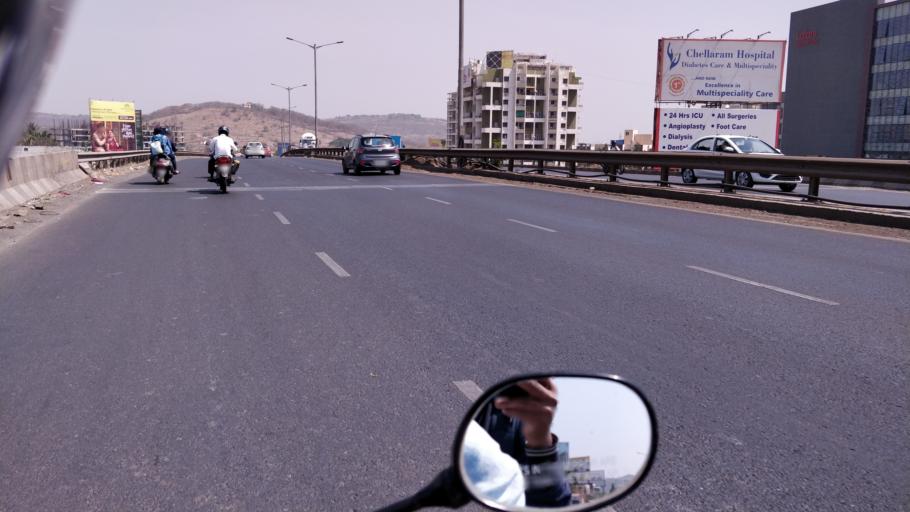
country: IN
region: Maharashtra
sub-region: Pune Division
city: Kharakvasla
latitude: 18.5193
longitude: 73.7689
